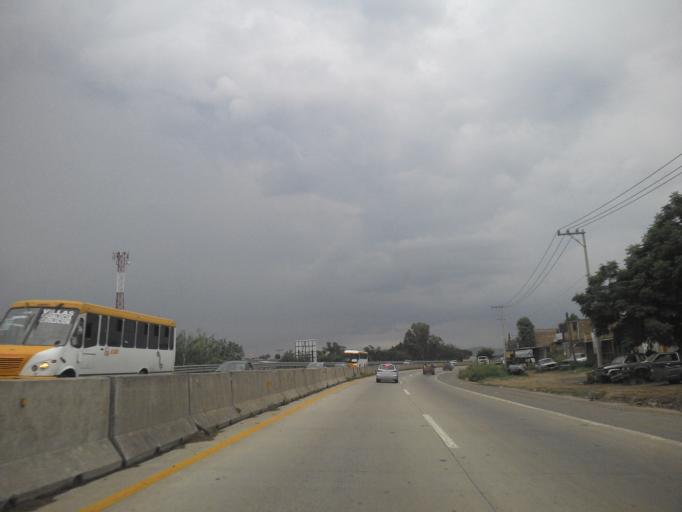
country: MX
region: Jalisco
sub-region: Tonala
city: Colonia Guadalupana
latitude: 20.5712
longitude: -103.2120
